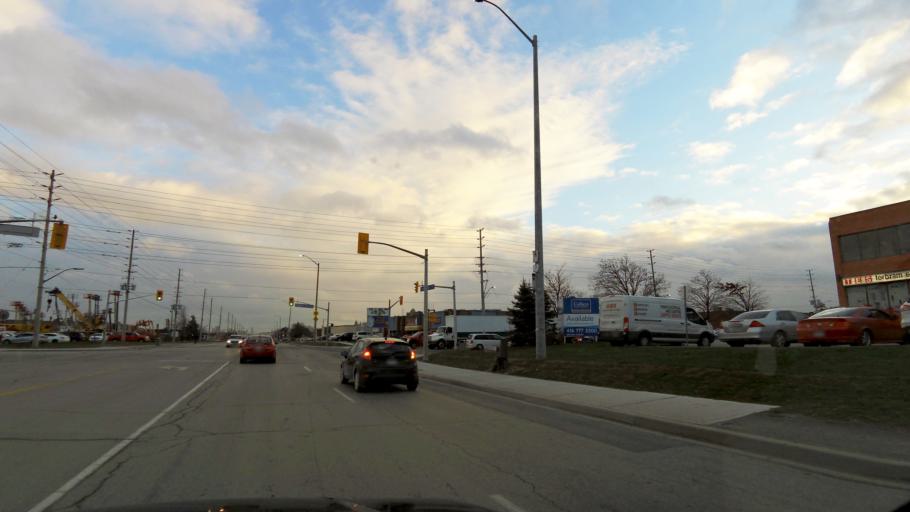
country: CA
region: Ontario
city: Etobicoke
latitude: 43.6995
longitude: -79.6599
